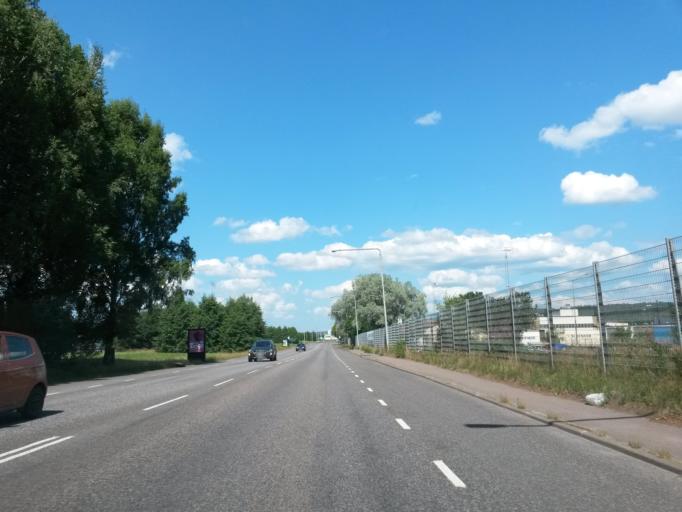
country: SE
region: Vaestra Goetaland
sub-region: Goteborg
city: Hammarkullen
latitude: 57.7630
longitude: 11.9942
